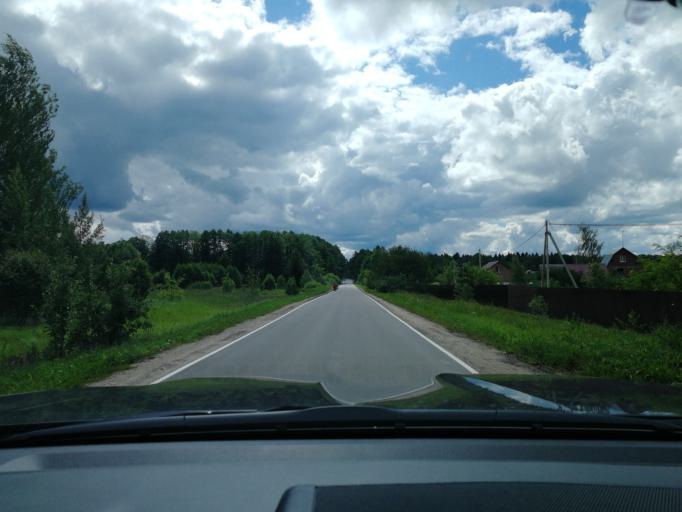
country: RU
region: Moskovskaya
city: Proletarskiy
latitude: 55.0119
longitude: 37.4811
